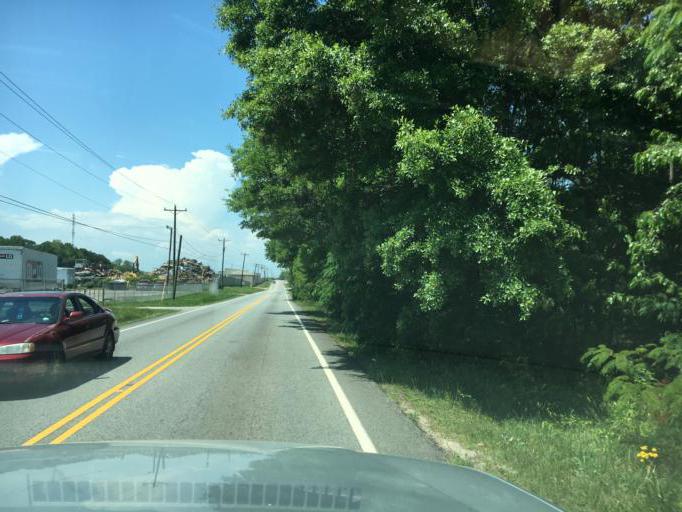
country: US
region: South Carolina
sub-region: Spartanburg County
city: Saxon
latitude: 34.9709
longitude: -81.9652
